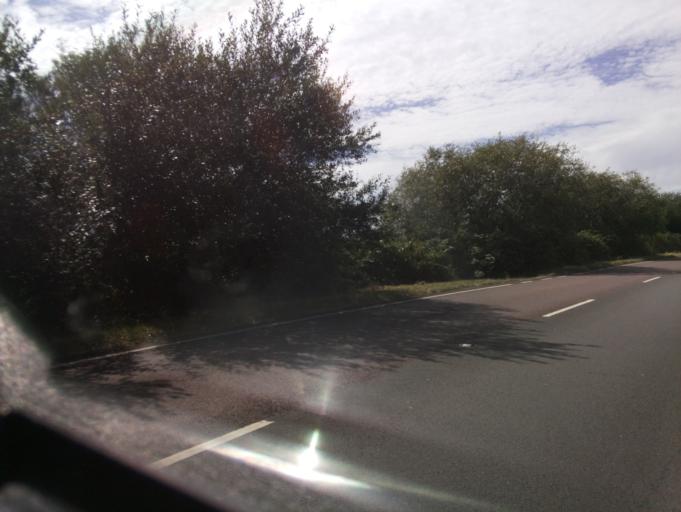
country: GB
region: England
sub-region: Dorset
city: Dorchester
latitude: 50.7229
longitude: -2.4548
